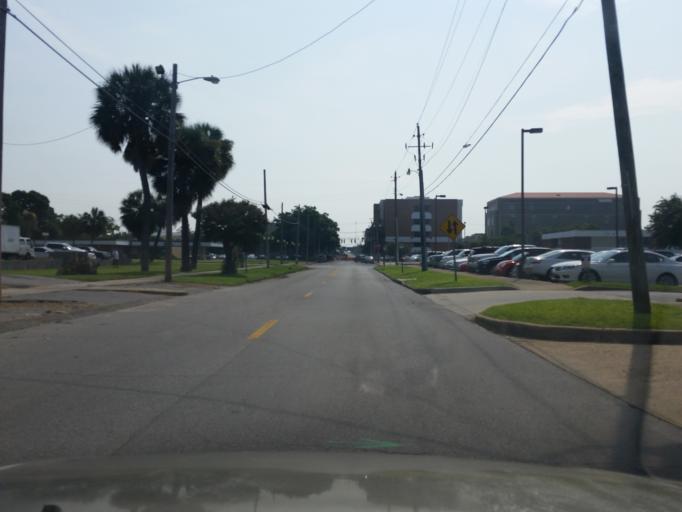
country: US
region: Florida
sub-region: Escambia County
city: Pensacola
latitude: 30.4136
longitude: -87.2195
